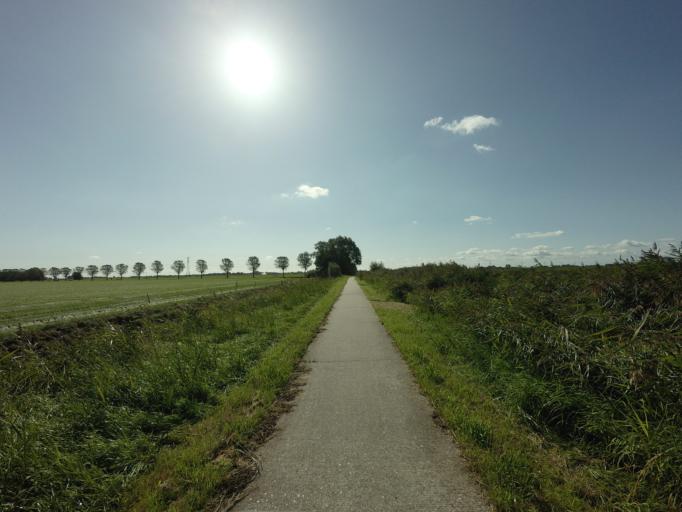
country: NL
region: Friesland
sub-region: Gemeente Boarnsterhim
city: Reduzum
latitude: 53.1216
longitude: 5.7560
